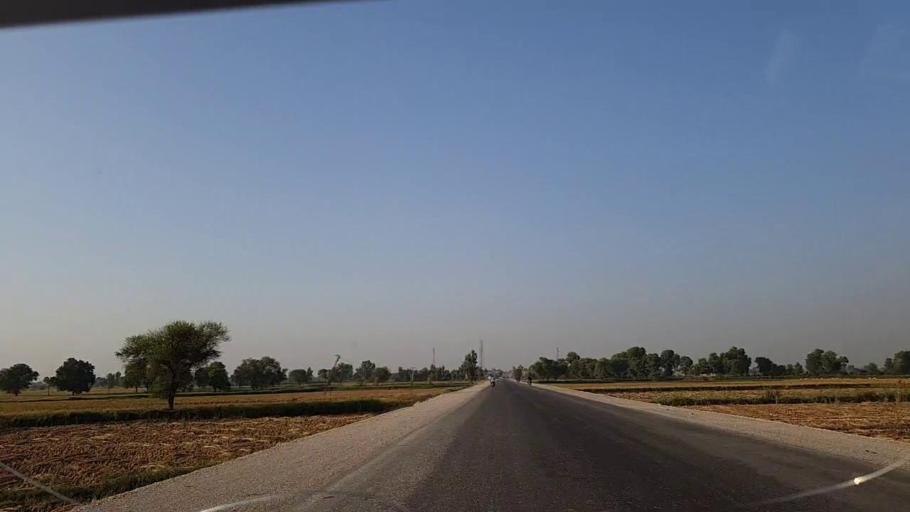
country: PK
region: Sindh
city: Rustam jo Goth
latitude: 27.9560
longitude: 68.8078
